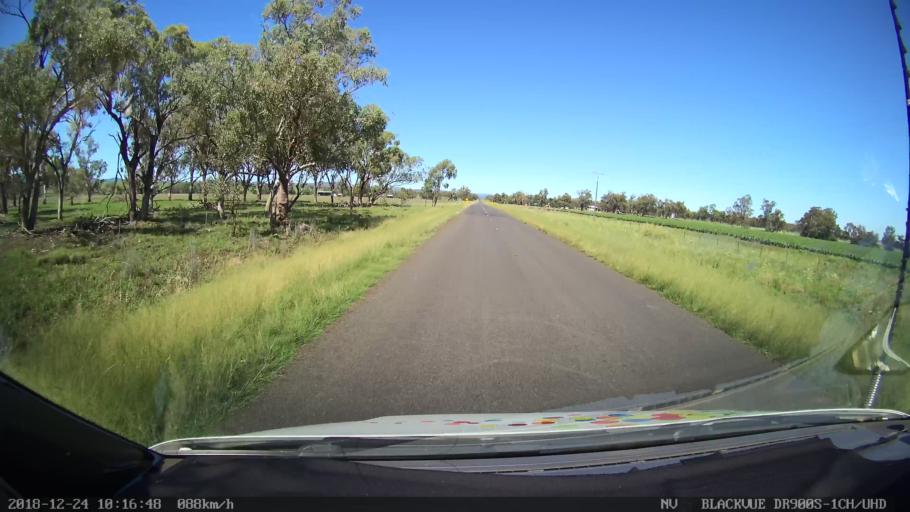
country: AU
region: New South Wales
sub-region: Liverpool Plains
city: Quirindi
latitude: -31.7176
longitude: 150.6007
